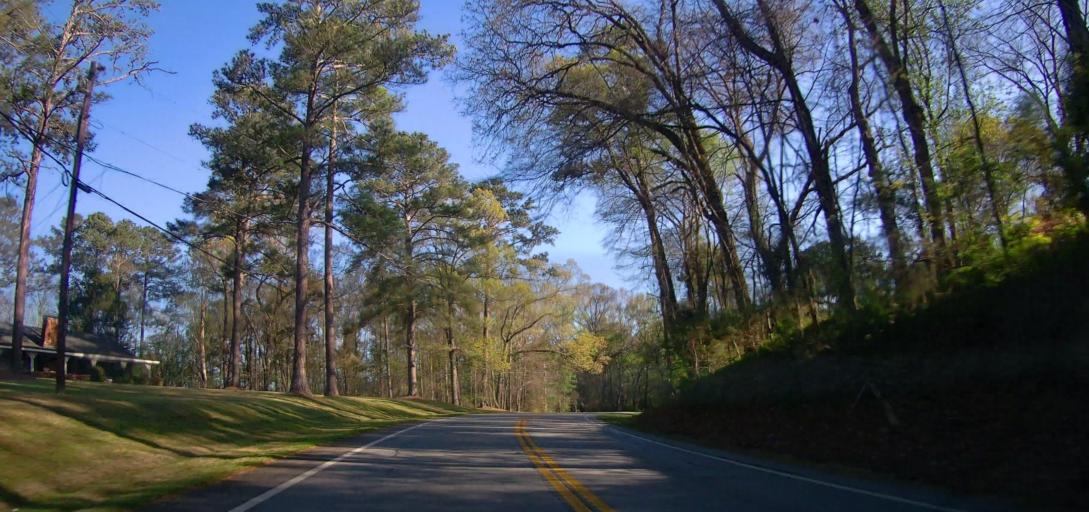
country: US
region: Georgia
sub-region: Butts County
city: Indian Springs
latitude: 33.2386
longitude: -83.9208
